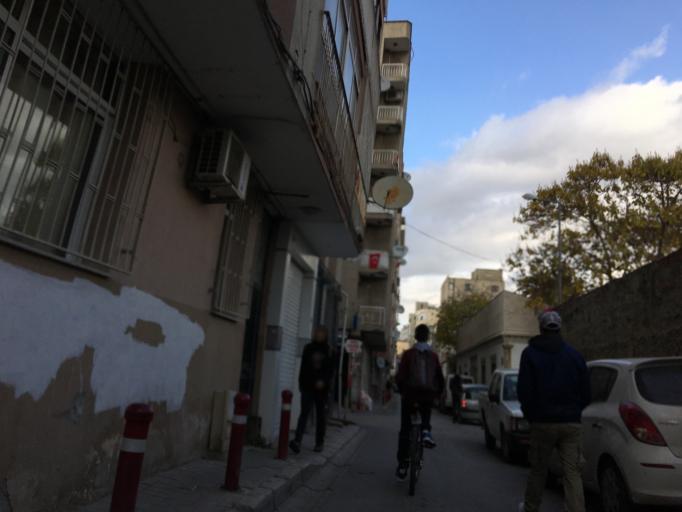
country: TR
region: Izmir
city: Izmir
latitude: 38.4376
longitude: 27.1468
